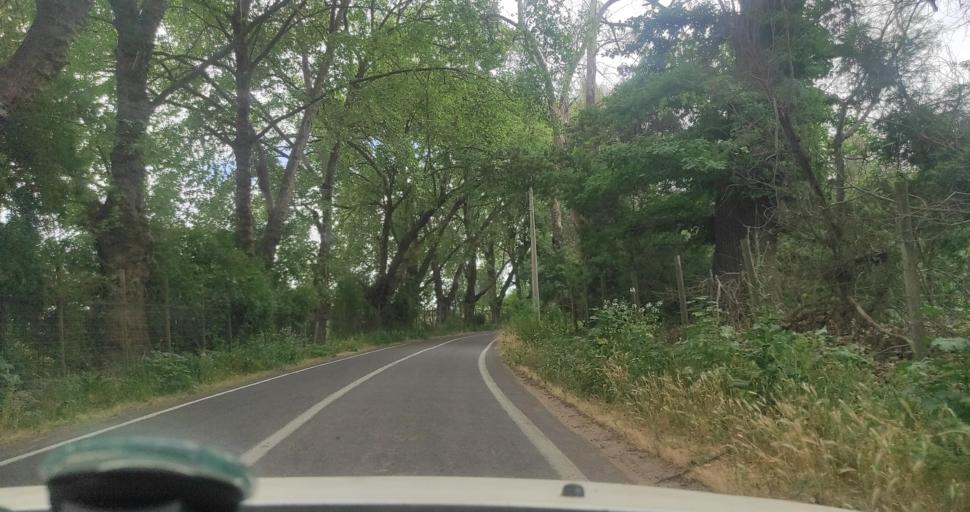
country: CL
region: Valparaiso
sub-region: Provincia de Marga Marga
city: Limache
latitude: -33.0241
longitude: -71.2411
